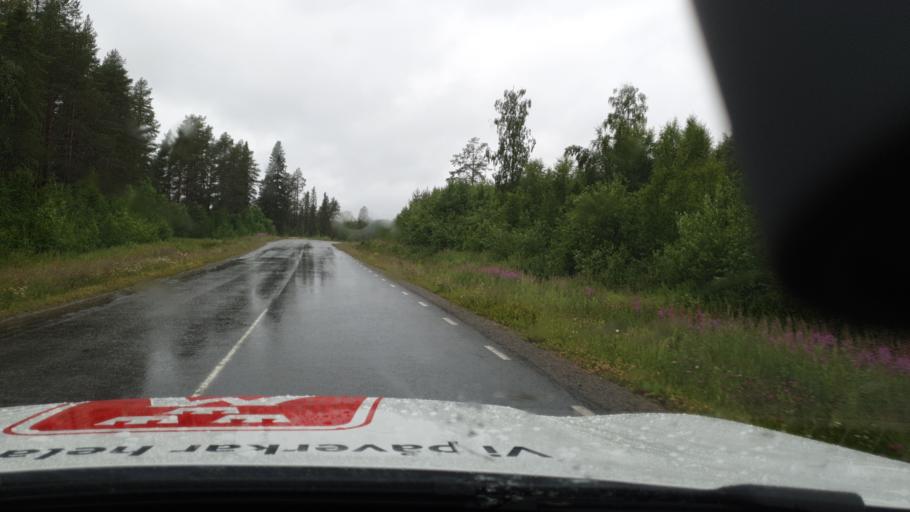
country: SE
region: Vaesterbotten
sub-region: Norsjo Kommun
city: Norsjoe
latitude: 64.8372
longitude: 19.8099
